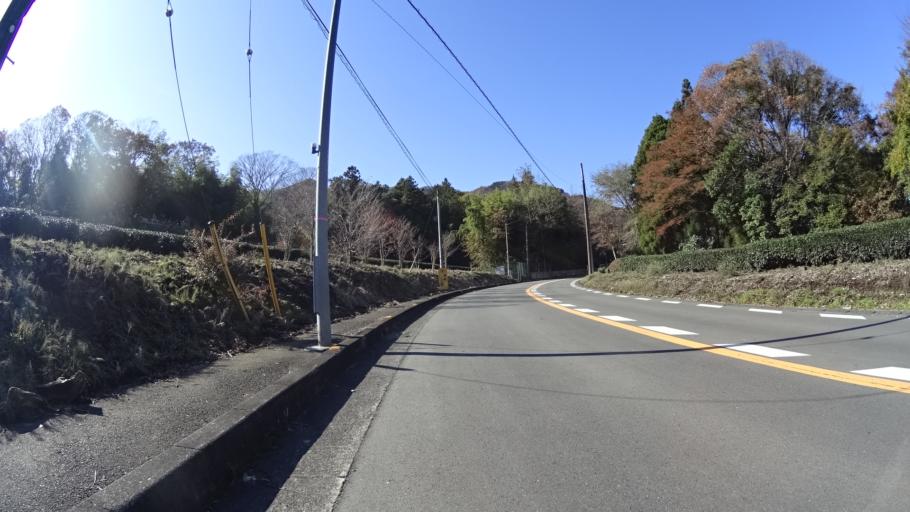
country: JP
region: Kanagawa
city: Zama
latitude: 35.5285
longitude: 139.2750
